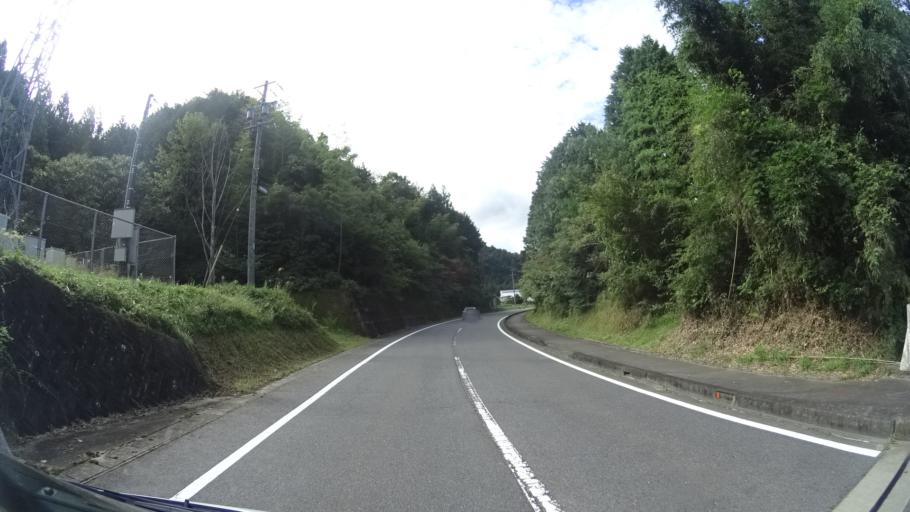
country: JP
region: Gifu
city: Minokamo
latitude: 35.5764
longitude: 137.0907
